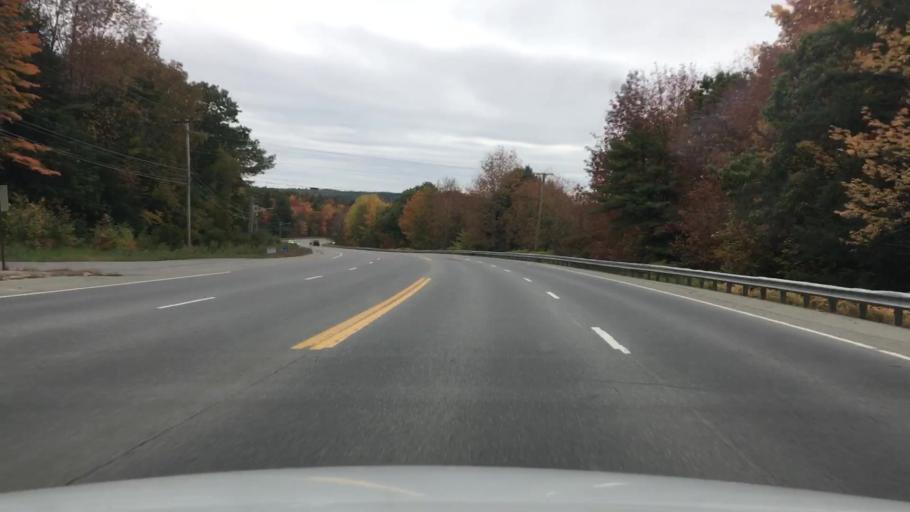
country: US
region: Maine
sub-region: Kennebec County
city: Oakland
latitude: 44.5456
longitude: -69.6996
